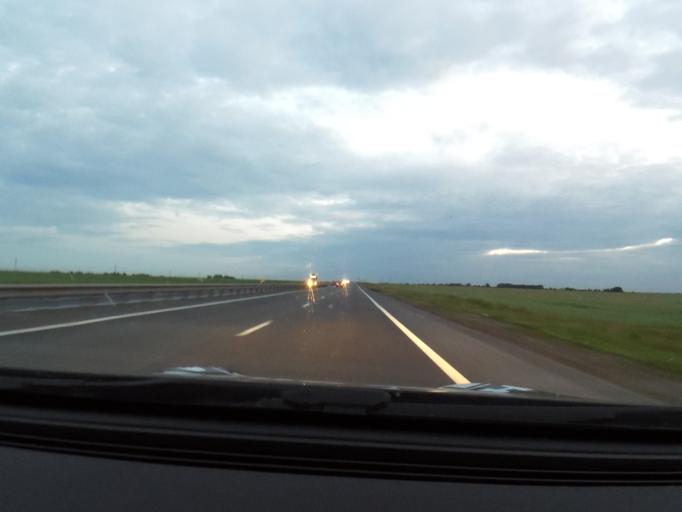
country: RU
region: Chuvashia
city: Yadrin
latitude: 56.0086
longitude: 46.2232
